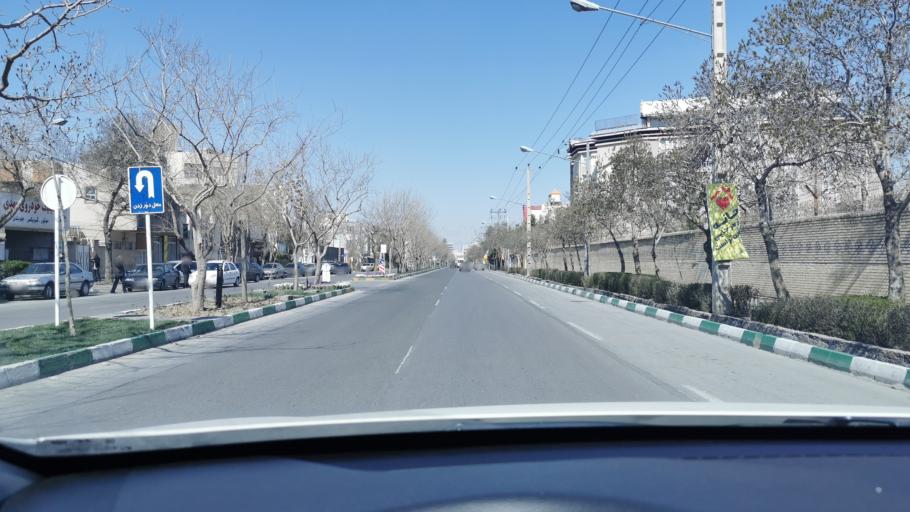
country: IR
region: Razavi Khorasan
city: Mashhad
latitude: 36.2788
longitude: 59.5770
